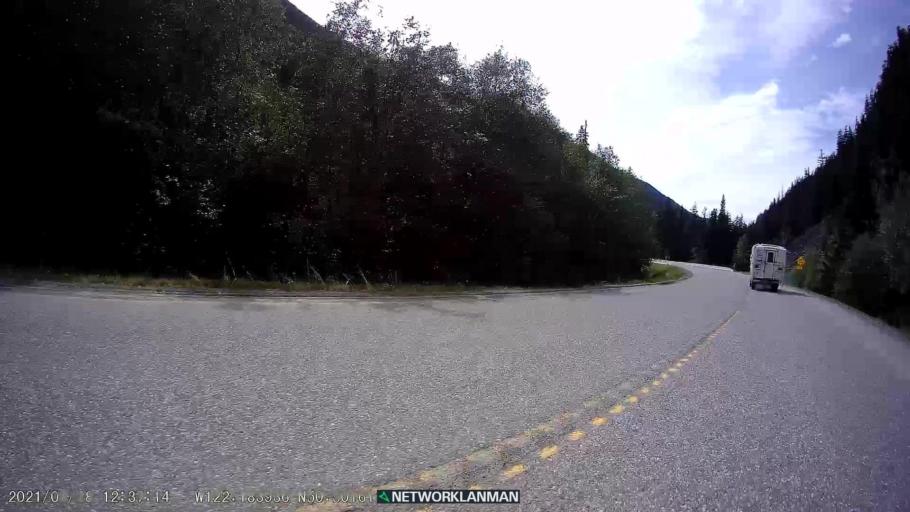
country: CA
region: British Columbia
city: Lillooet
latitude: 50.5015
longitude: -122.1846
